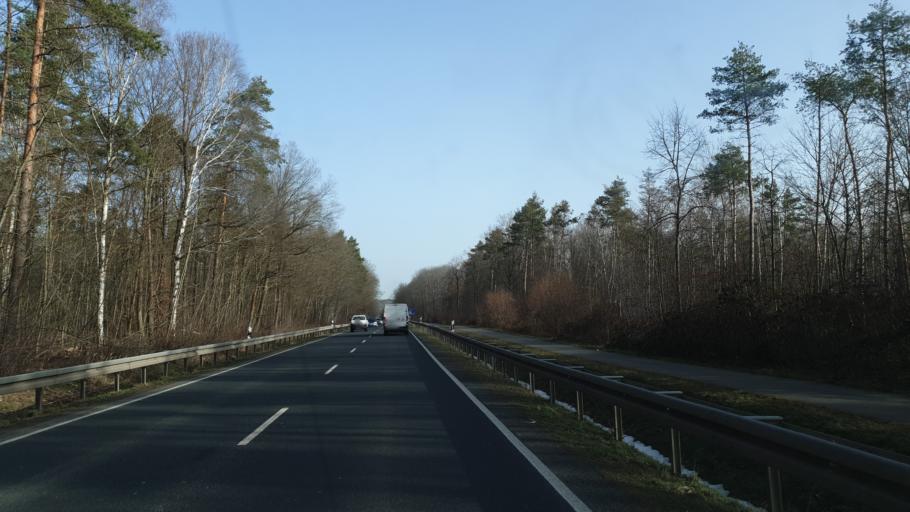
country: DE
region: Saxony
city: Naunhof
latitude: 51.2966
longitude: 12.5945
